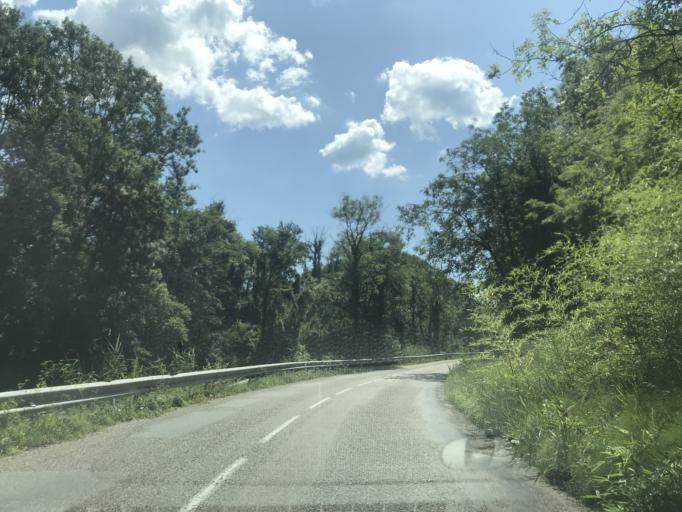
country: FR
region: Rhone-Alpes
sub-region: Departement de la Savoie
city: Chatillon
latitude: 45.8159
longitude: 5.8130
